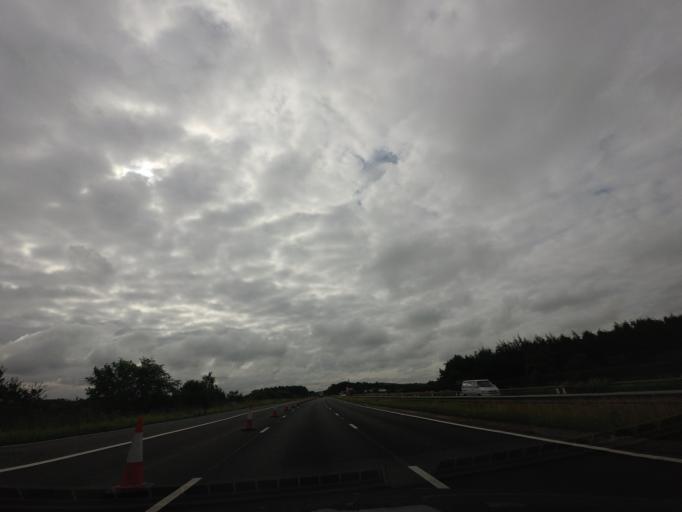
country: GB
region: Scotland
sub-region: Dumfries and Galloway
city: Gretna
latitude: 54.9720
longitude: -3.0050
